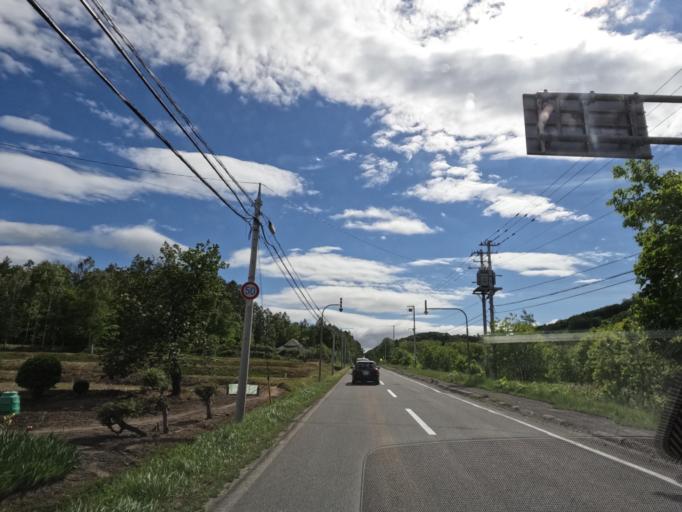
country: JP
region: Hokkaido
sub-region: Asahikawa-shi
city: Asahikawa
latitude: 43.8388
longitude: 142.5426
